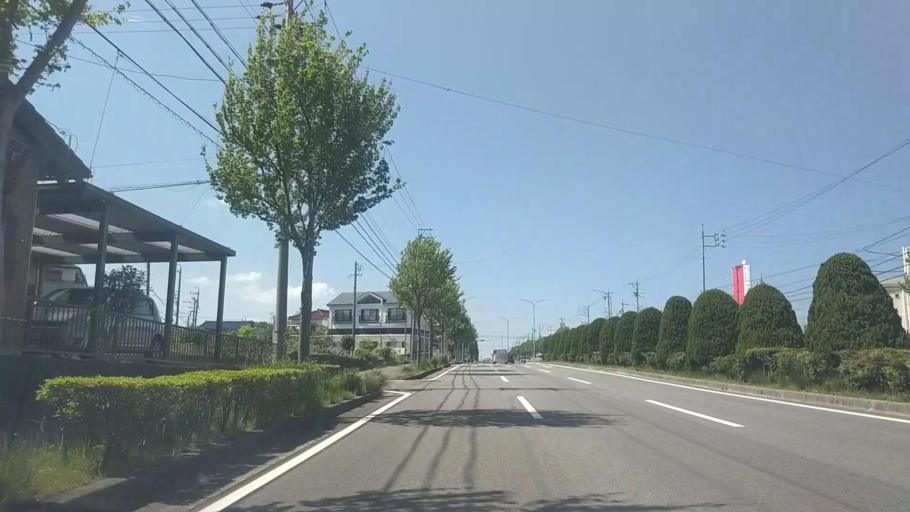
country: JP
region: Aichi
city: Okazaki
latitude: 34.9696
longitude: 137.1808
